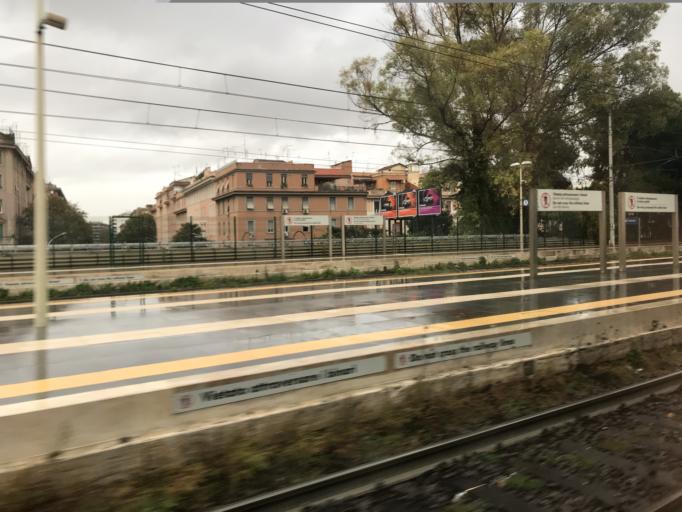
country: VA
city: Vatican City
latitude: 41.8724
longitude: 12.4673
